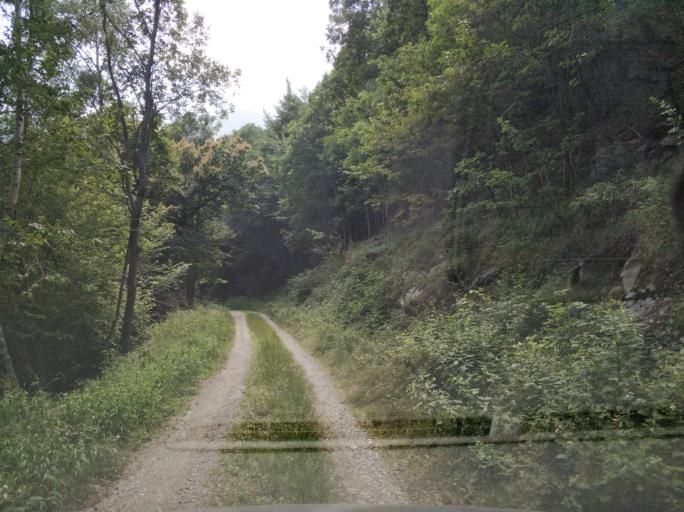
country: IT
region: Piedmont
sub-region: Provincia di Torino
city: Ceres
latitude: 45.3108
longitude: 7.3623
